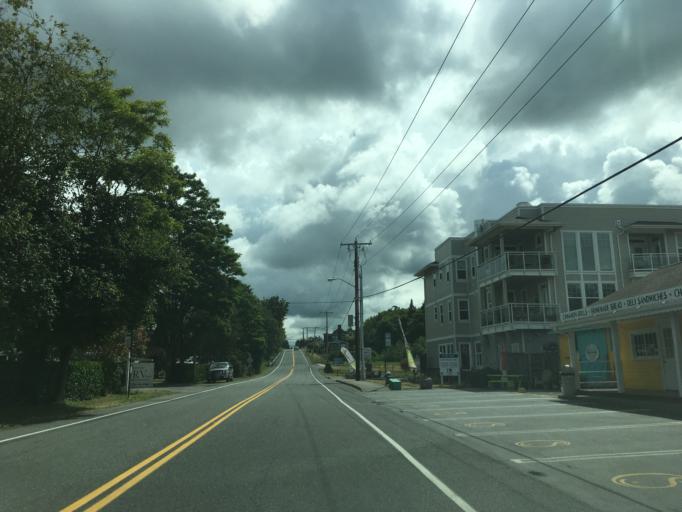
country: US
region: Washington
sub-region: Whatcom County
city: Birch Bay
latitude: 48.9178
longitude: -122.7447
